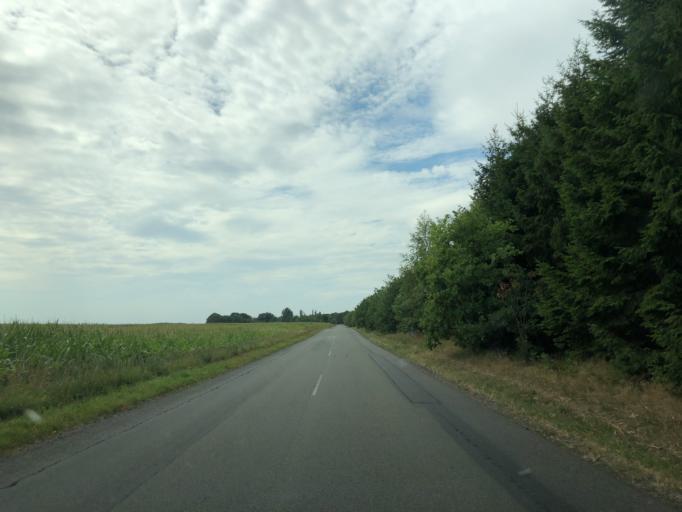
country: DK
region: South Denmark
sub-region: Vejle Kommune
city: Egtved
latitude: 55.6419
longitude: 9.2024
